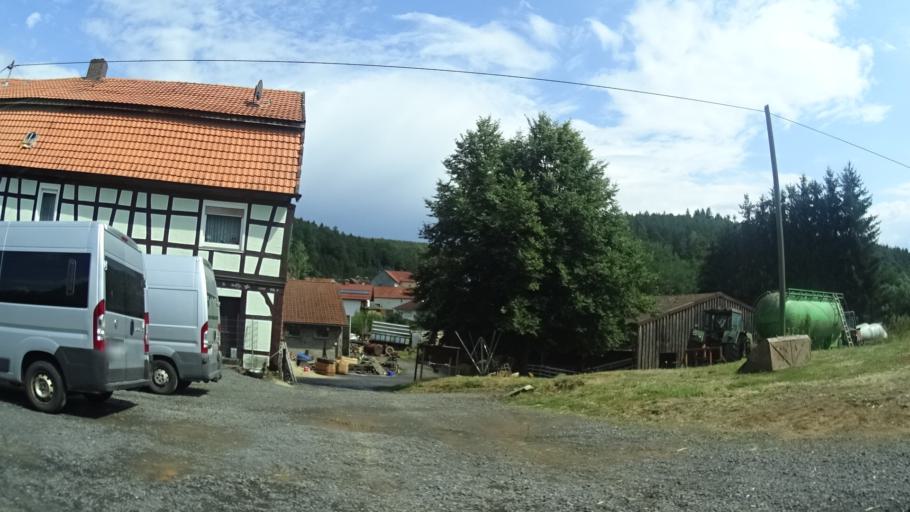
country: DE
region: Hesse
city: Grebenau
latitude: 50.7136
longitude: 9.4465
